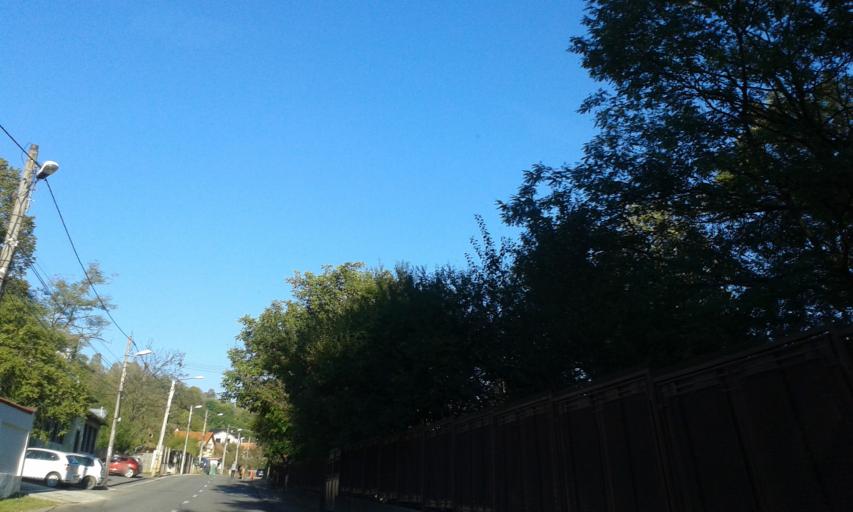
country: RO
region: Hunedoara
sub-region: Municipiul Petrosani
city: Petrosani
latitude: 45.4267
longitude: 23.3849
